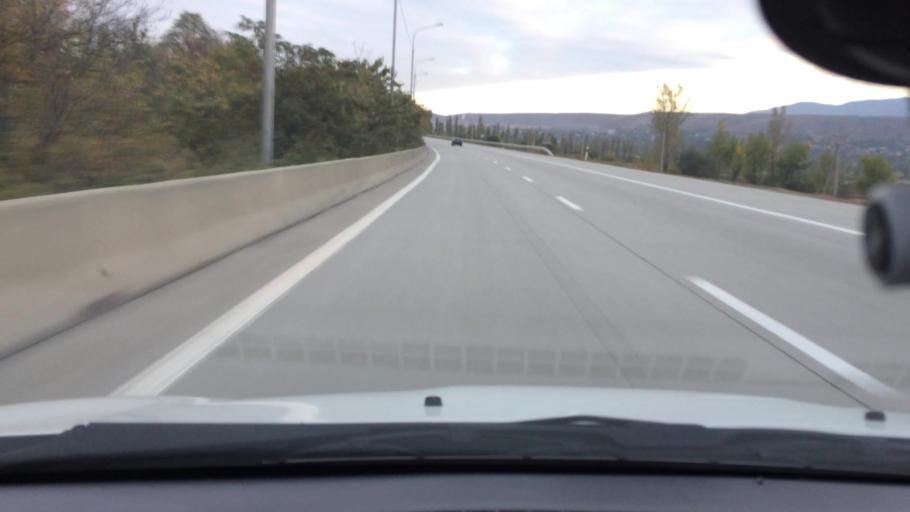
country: GE
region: Shida Kartli
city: Kaspi
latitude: 41.9553
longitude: 44.4913
